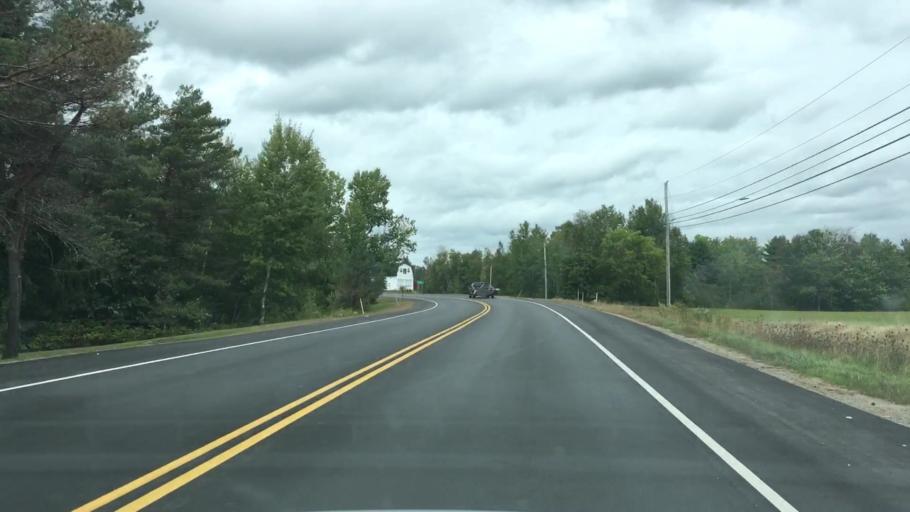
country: US
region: Maine
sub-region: Penobscot County
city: Milford
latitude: 44.9562
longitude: -68.7032
